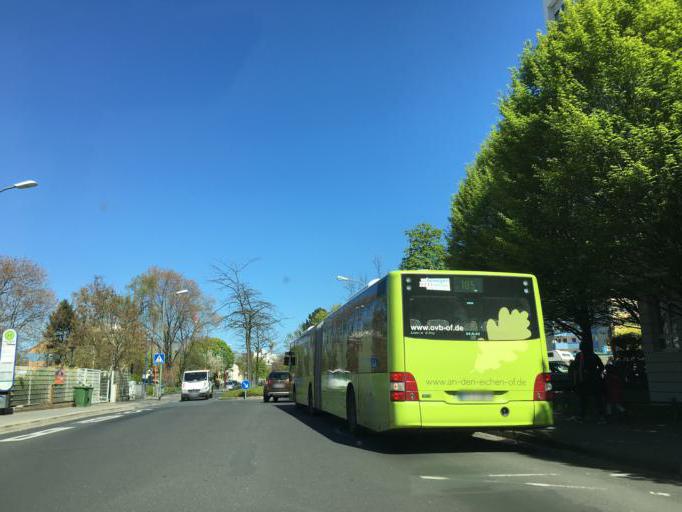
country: DE
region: Hesse
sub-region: Regierungsbezirk Darmstadt
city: Offenbach
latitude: 50.0885
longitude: 8.7543
